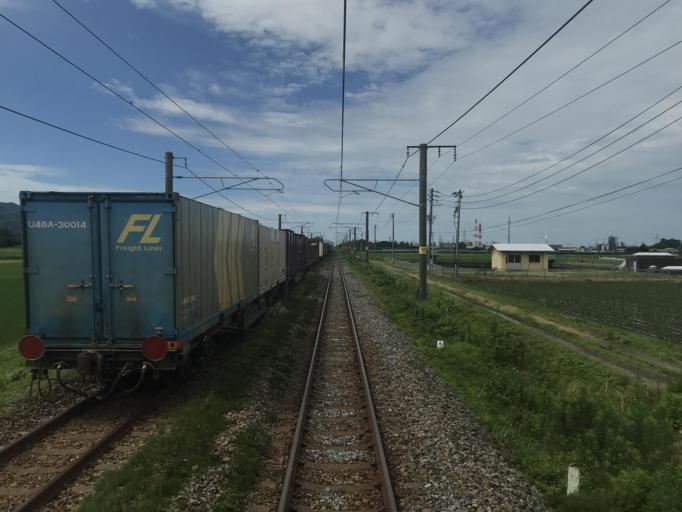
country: JP
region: Niigata
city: Shibata
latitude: 38.0782
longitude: 139.4170
